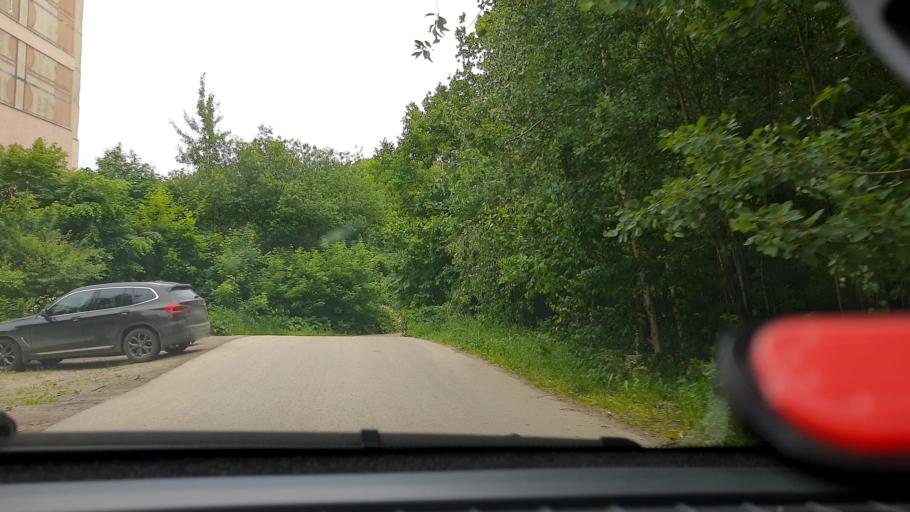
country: RU
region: Nizjnij Novgorod
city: Nizhniy Novgorod
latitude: 56.2291
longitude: 43.9367
